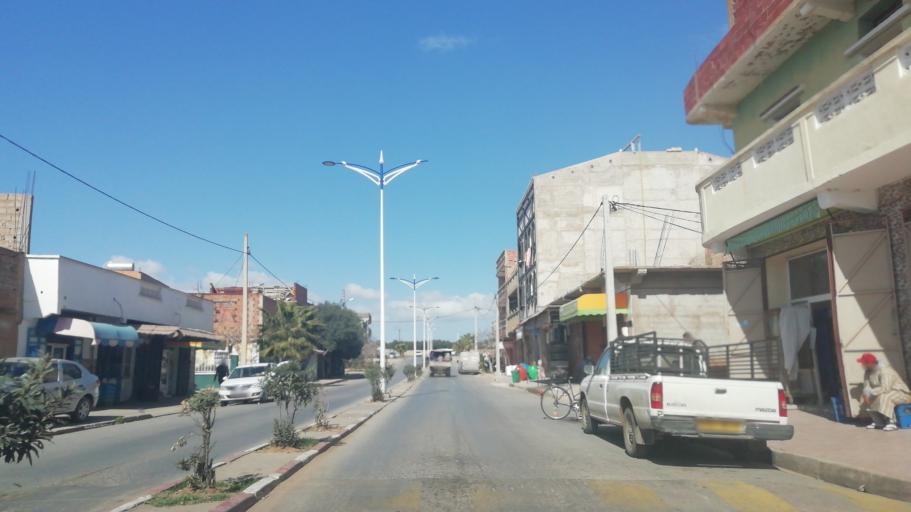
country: DZ
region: Mostaganem
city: Mostaganem
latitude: 35.9978
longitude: 0.3046
